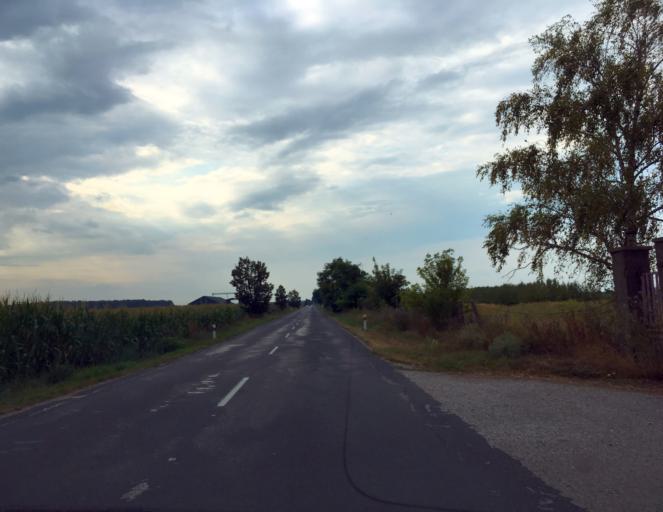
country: SK
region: Trnavsky
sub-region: Okres Dunajska Streda
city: Velky Meder
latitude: 47.9259
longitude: 17.7351
